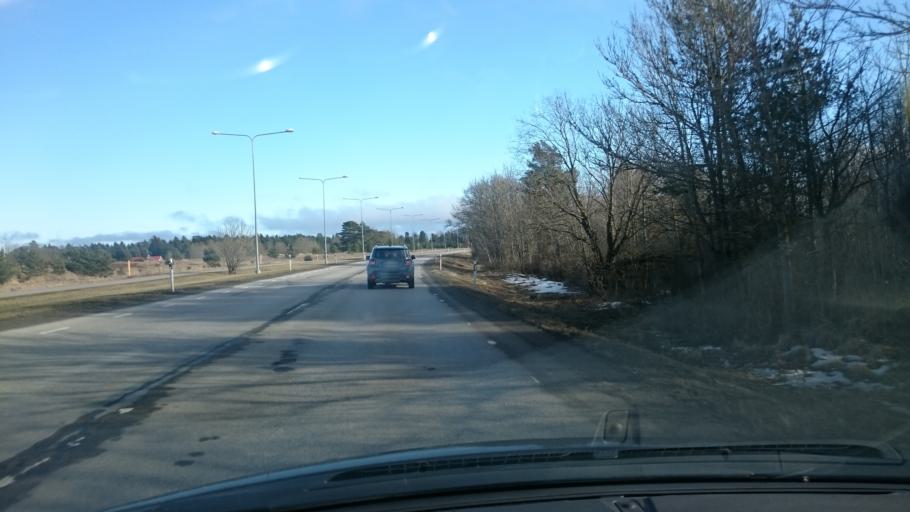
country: EE
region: Harju
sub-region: Harku vald
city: Tabasalu
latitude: 59.4420
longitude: 24.4911
